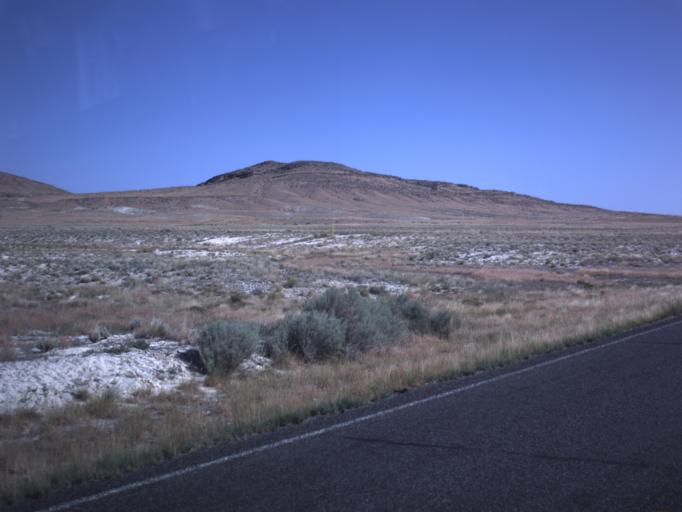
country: US
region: Utah
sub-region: Beaver County
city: Milford
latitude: 38.8649
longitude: -112.8373
